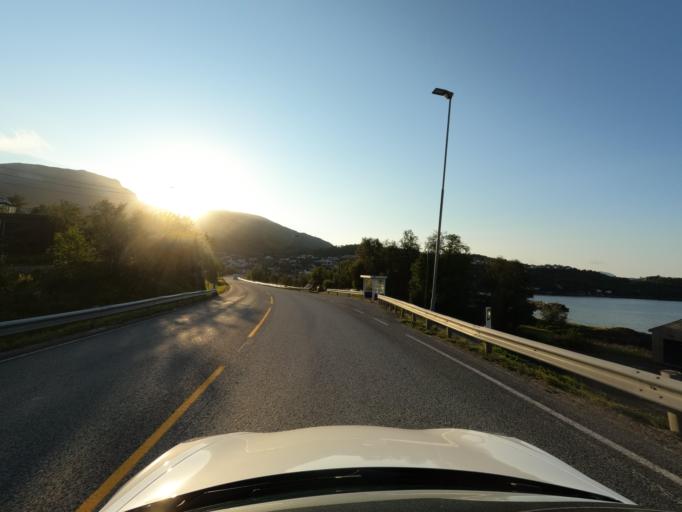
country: NO
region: Troms
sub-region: Harstad
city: Harstad
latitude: 68.7441
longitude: 16.5661
